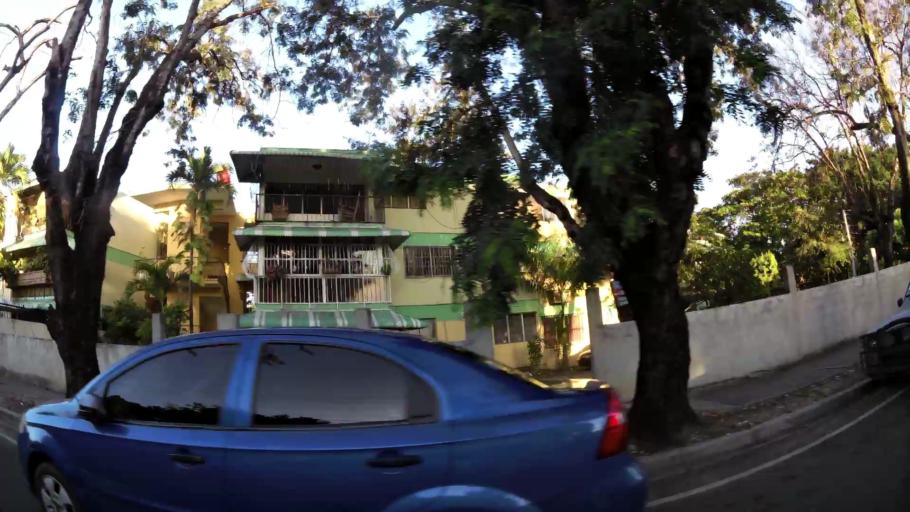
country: DO
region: Nacional
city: La Agustina
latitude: 18.4863
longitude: -69.9599
